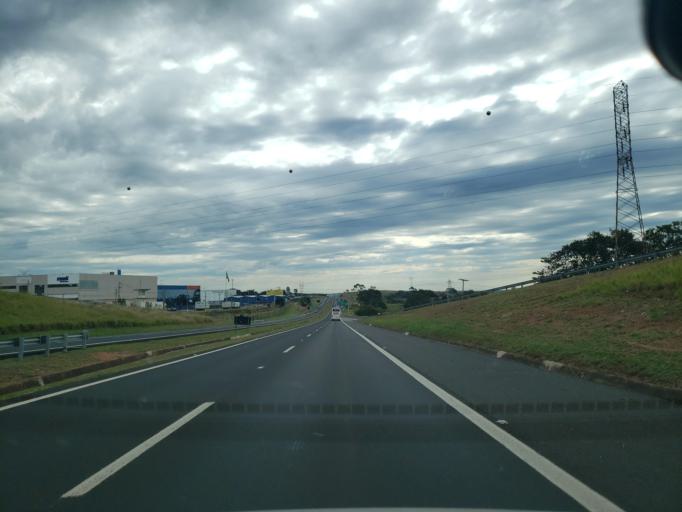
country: BR
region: Sao Paulo
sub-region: Bauru
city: Bauru
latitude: -22.2806
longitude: -49.0878
